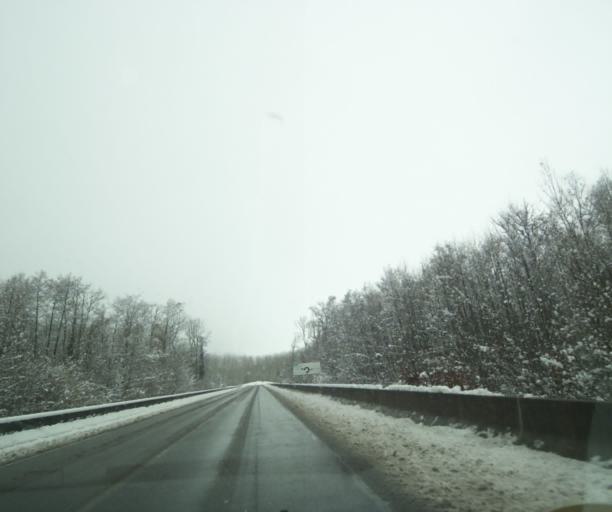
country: FR
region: Champagne-Ardenne
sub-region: Departement de la Haute-Marne
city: Villiers-en-Lieu
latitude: 48.5792
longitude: 4.8592
